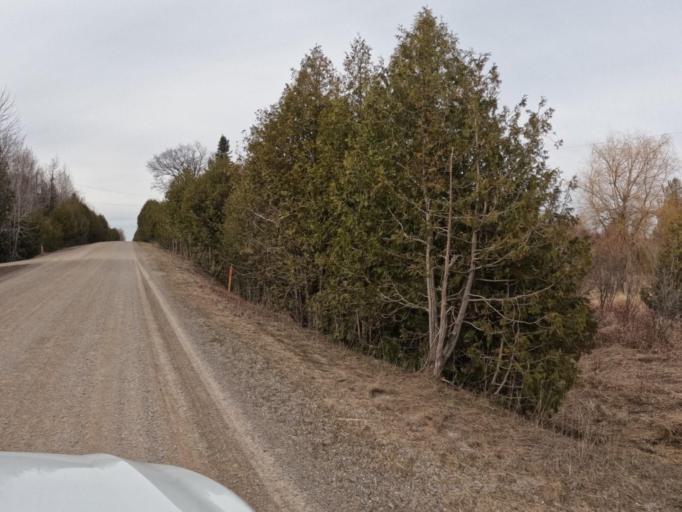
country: CA
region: Ontario
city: Orangeville
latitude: 43.9282
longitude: -80.2572
